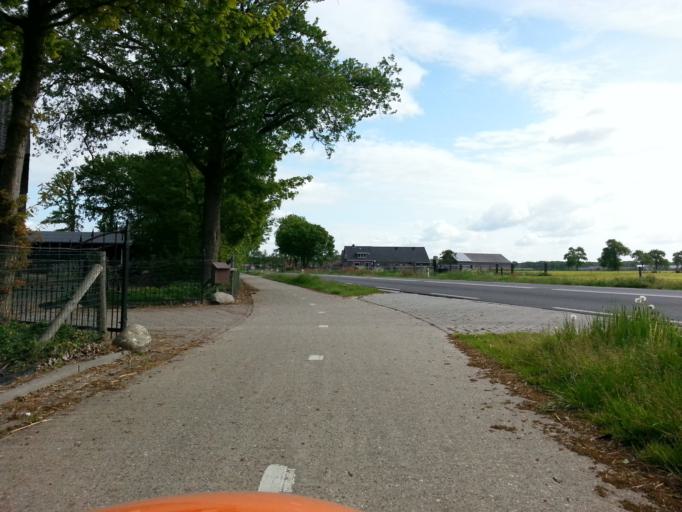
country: NL
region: Utrecht
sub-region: Gemeente Utrechtse Heuvelrug
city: Overberg
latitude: 52.0922
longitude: 5.5122
